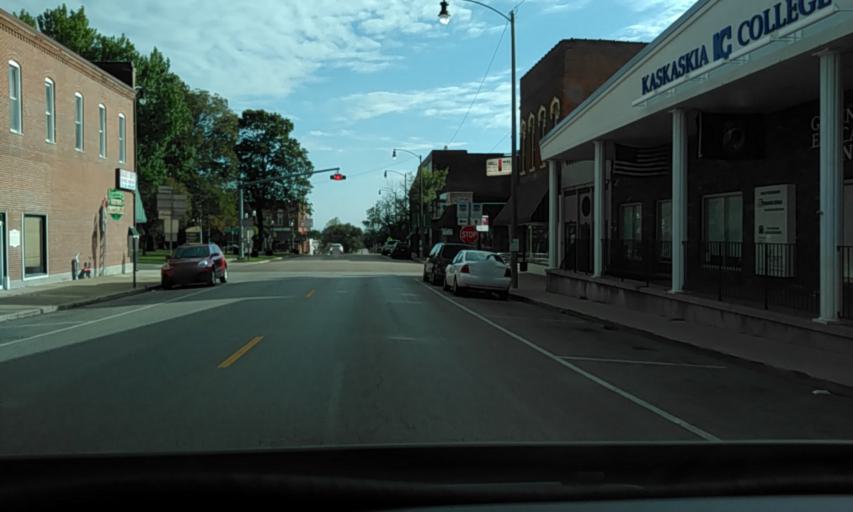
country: US
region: Illinois
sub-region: Bond County
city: Greenville
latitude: 38.8932
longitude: -89.4135
